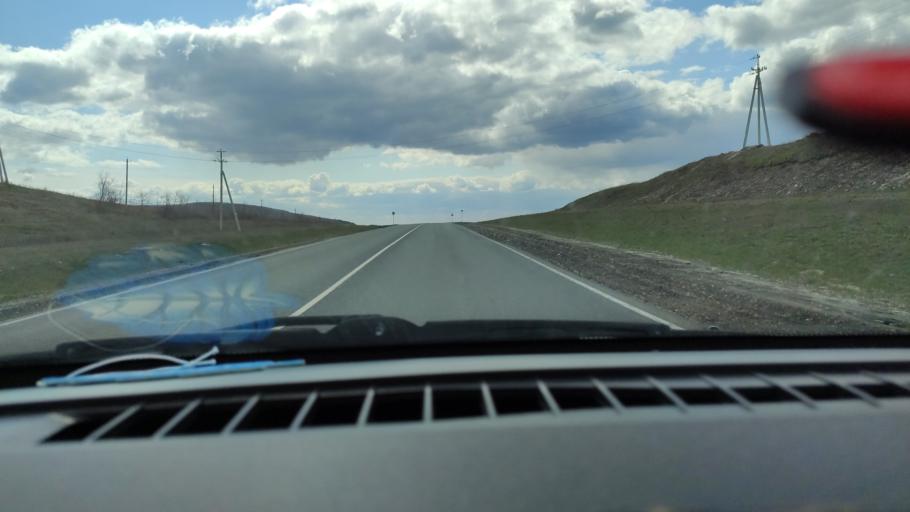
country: RU
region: Saratov
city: Alekseyevka
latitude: 52.3170
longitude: 47.9227
